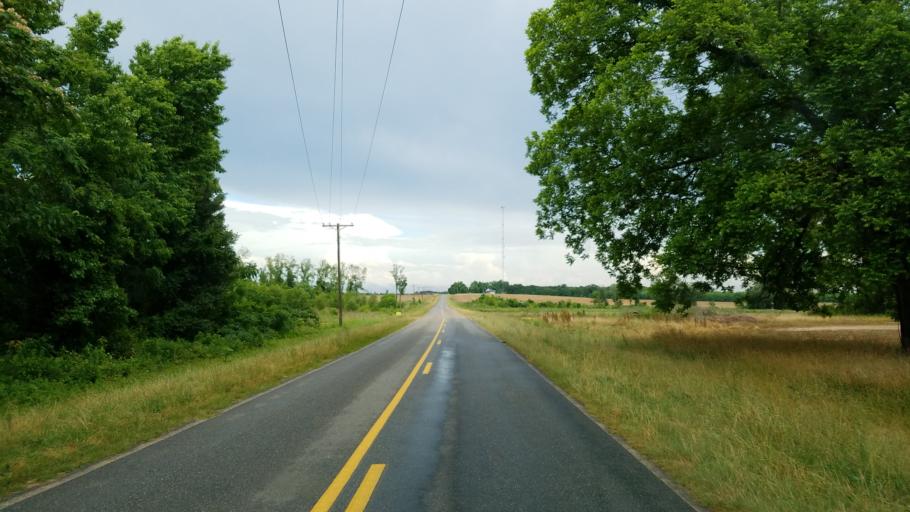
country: US
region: Georgia
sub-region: Dooly County
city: Vienna
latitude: 32.1623
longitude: -83.7988
